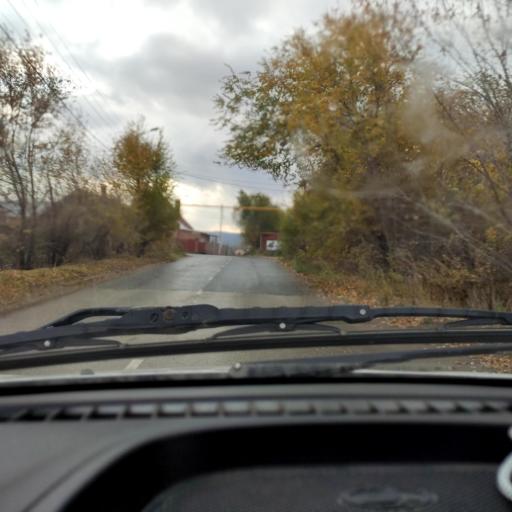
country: RU
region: Samara
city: Zhigulevsk
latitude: 53.4656
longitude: 49.6207
